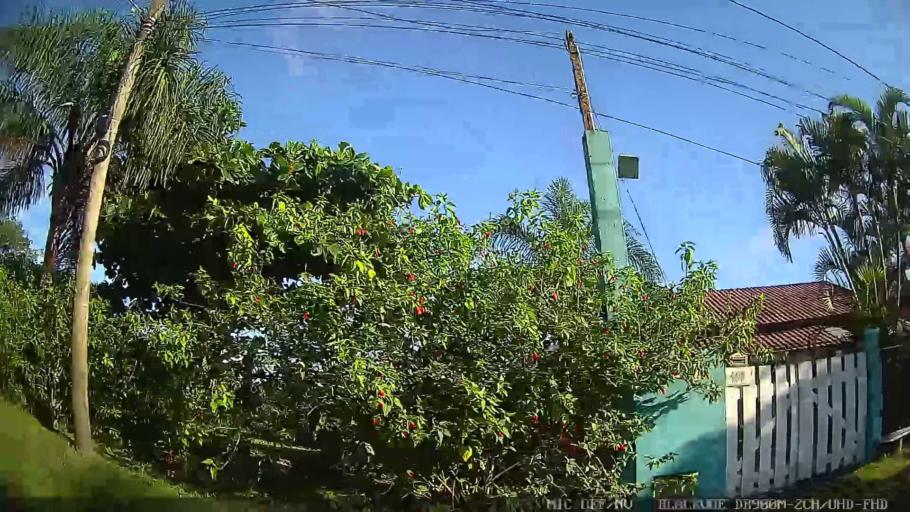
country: BR
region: Sao Paulo
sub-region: Iguape
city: Iguape
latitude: -24.7553
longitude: -47.5705
